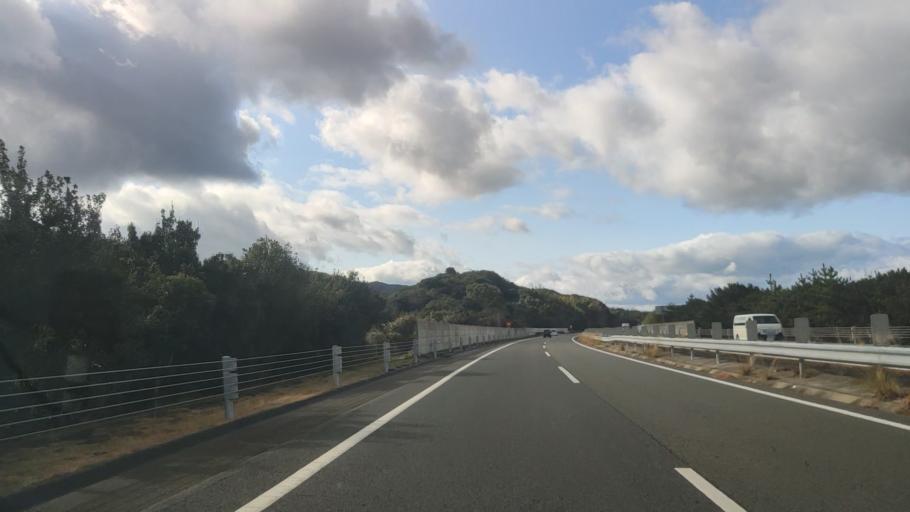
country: JP
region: Hyogo
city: Fukura
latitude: 34.2990
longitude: 134.7388
